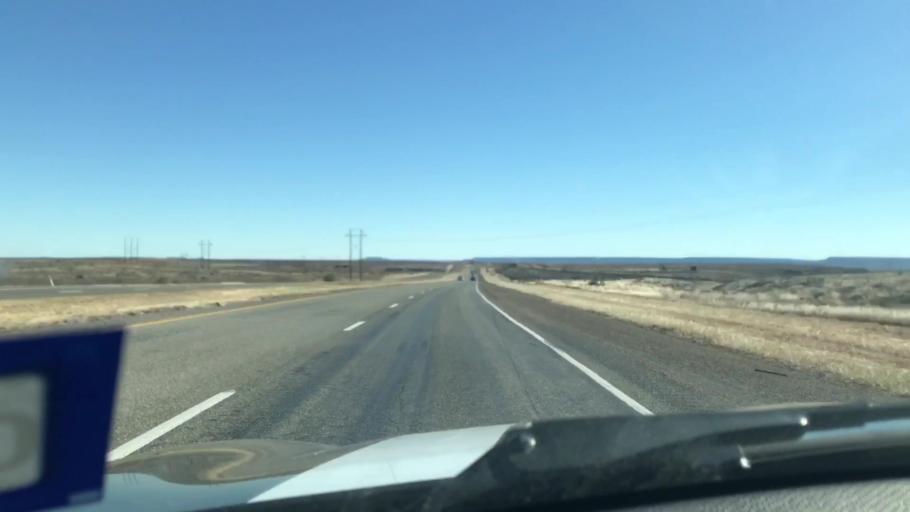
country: US
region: Texas
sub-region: Garza County
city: Post
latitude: 33.1178
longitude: -101.2785
